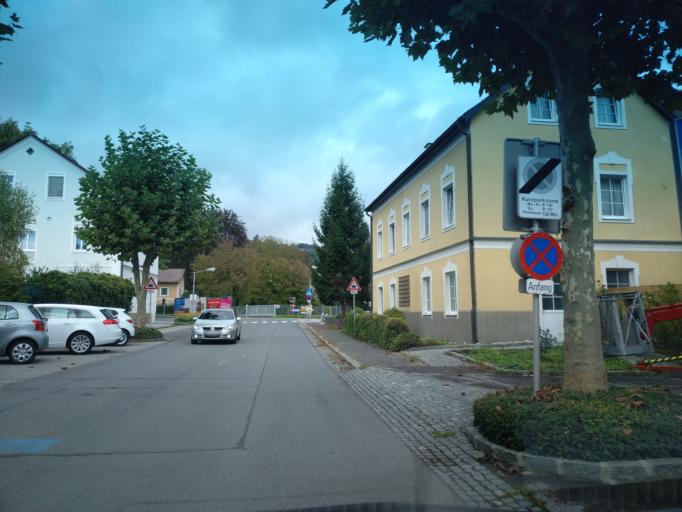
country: AT
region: Styria
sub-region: Politischer Bezirk Deutschlandsberg
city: Deutschlandsberg
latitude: 46.8174
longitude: 15.2149
